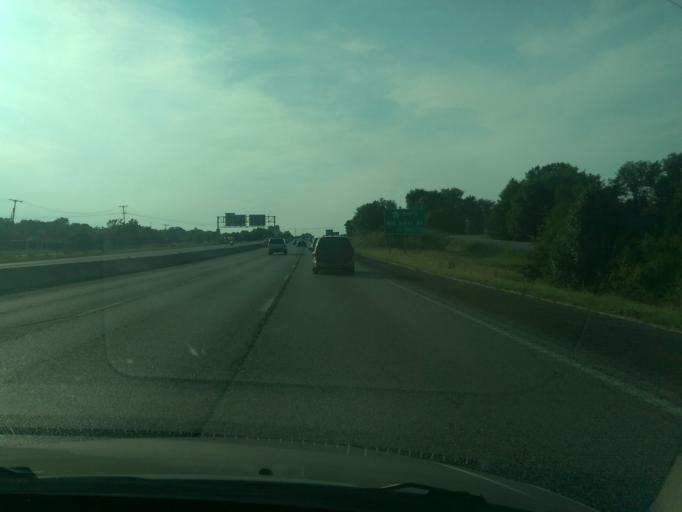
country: US
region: Missouri
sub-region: Platte County
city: Riverside
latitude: 39.2021
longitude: -94.6291
